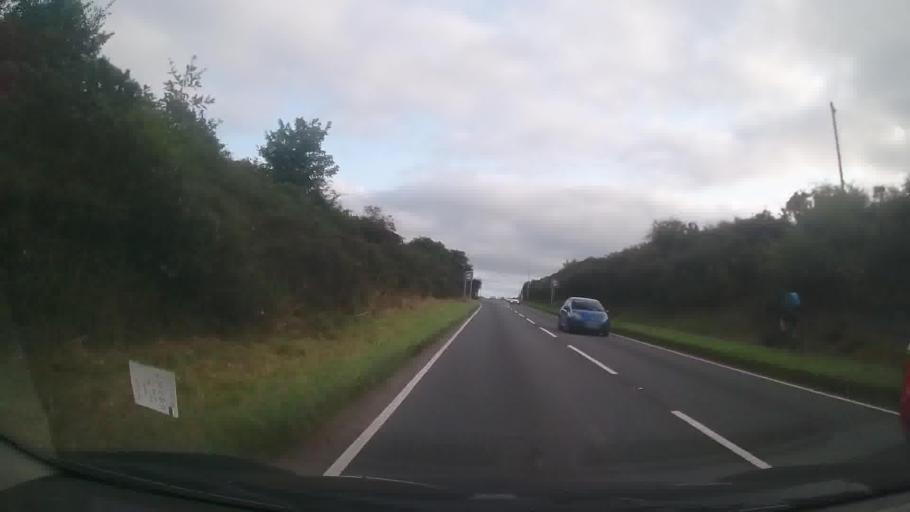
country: GB
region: Wales
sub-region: Pembrokeshire
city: Neyland
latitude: 51.7130
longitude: -4.9369
